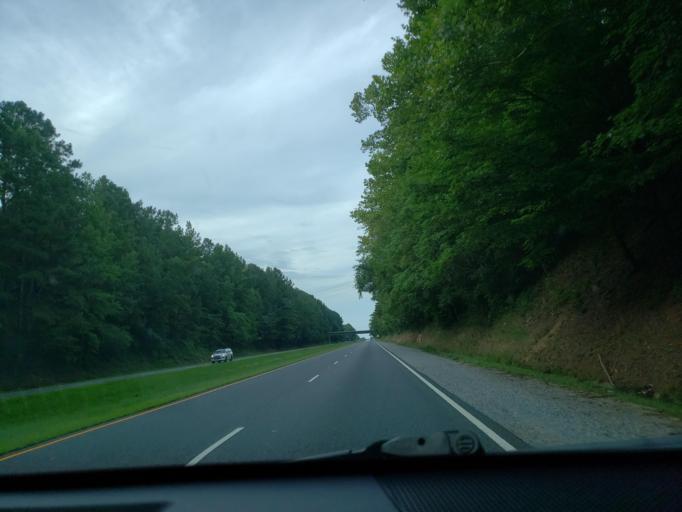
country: US
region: Virginia
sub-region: Brunswick County
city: Lawrenceville
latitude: 36.7547
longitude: -77.8333
